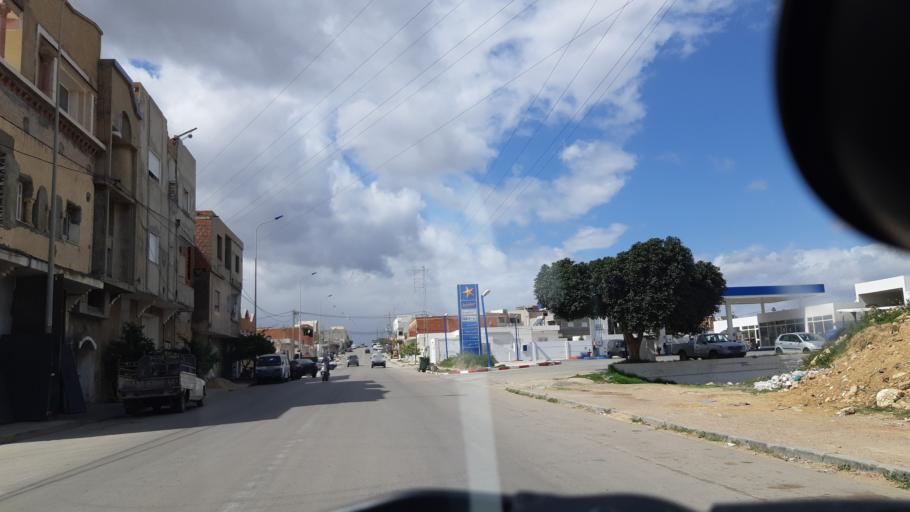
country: TN
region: Susah
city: Akouda
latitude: 35.8792
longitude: 10.5182
